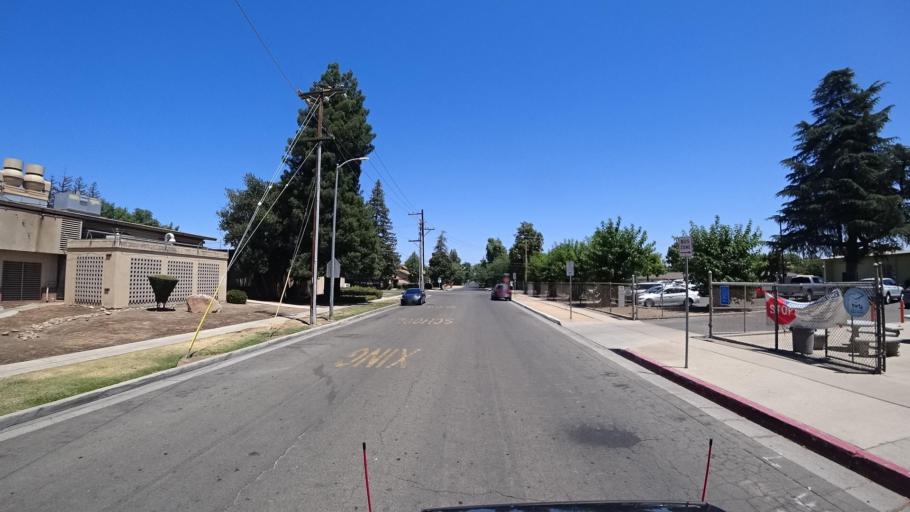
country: US
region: California
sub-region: Fresno County
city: Fresno
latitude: 36.7934
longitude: -119.7951
